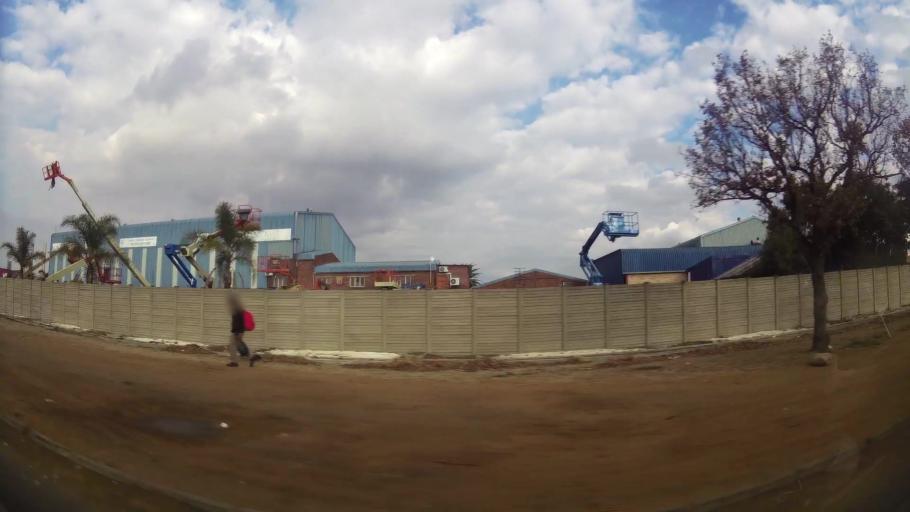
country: ZA
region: Orange Free State
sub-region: Fezile Dabi District Municipality
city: Sasolburg
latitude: -26.8221
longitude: 27.8336
